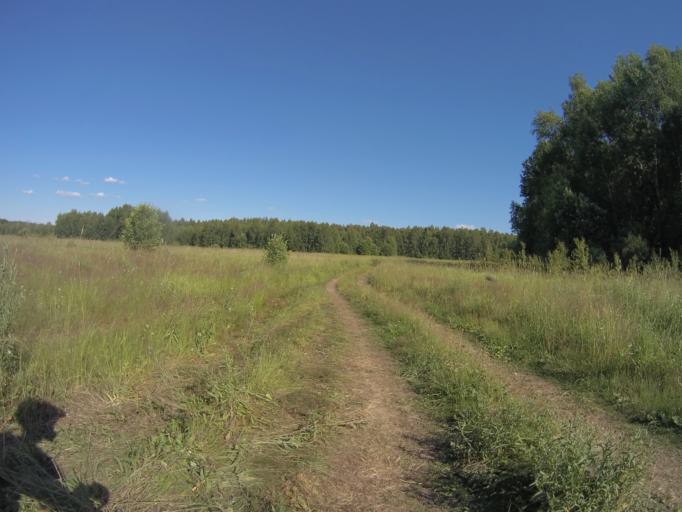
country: RU
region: Vladimir
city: Golovino
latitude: 55.9986
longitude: 40.4017
